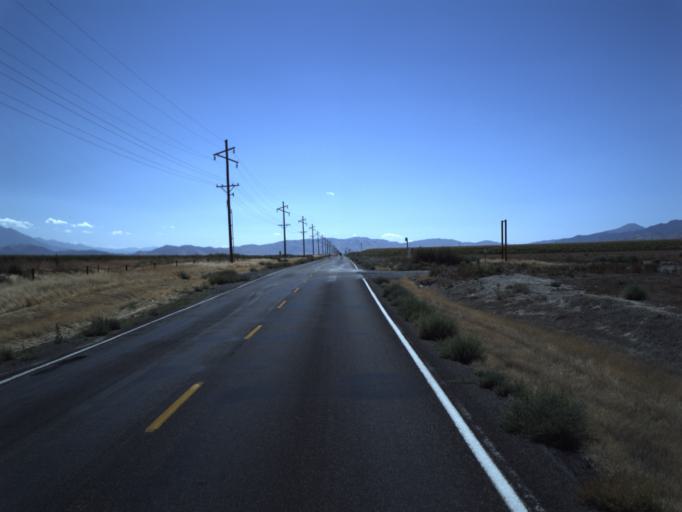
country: US
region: Utah
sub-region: Utah County
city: Genola
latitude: 40.0986
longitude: -111.9591
